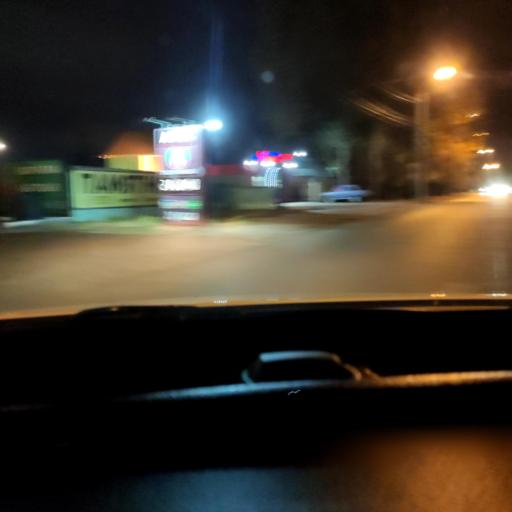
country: RU
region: Voronezj
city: Voronezh
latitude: 51.6457
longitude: 39.2673
